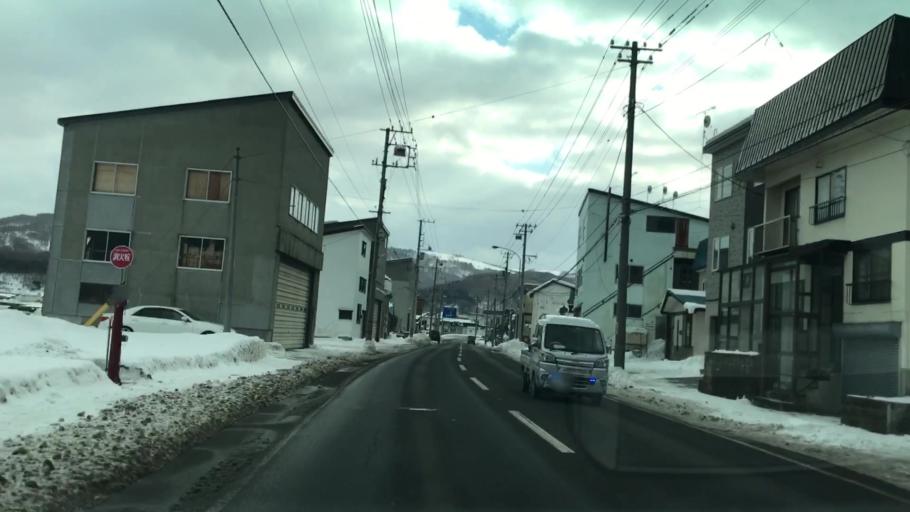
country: JP
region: Hokkaido
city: Yoichi
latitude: 43.2683
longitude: 140.6383
